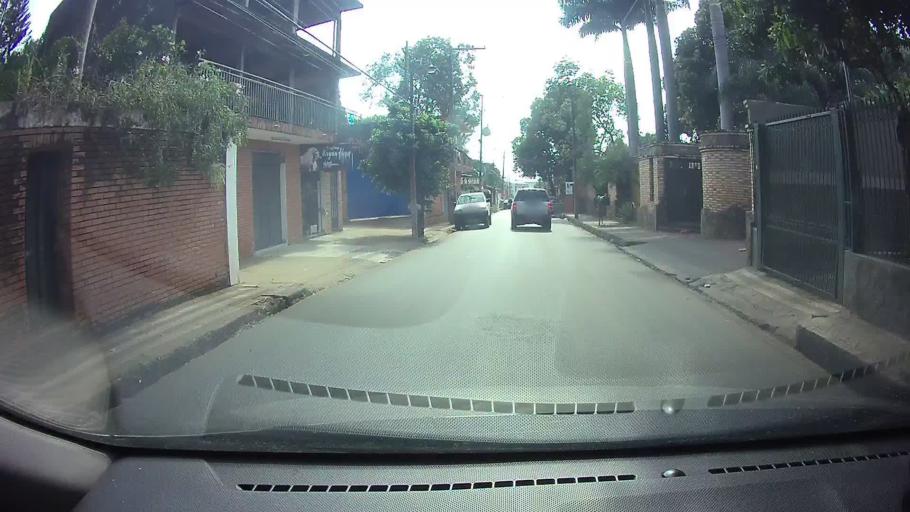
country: PY
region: Central
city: Fernando de la Mora
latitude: -25.3172
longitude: -57.5559
